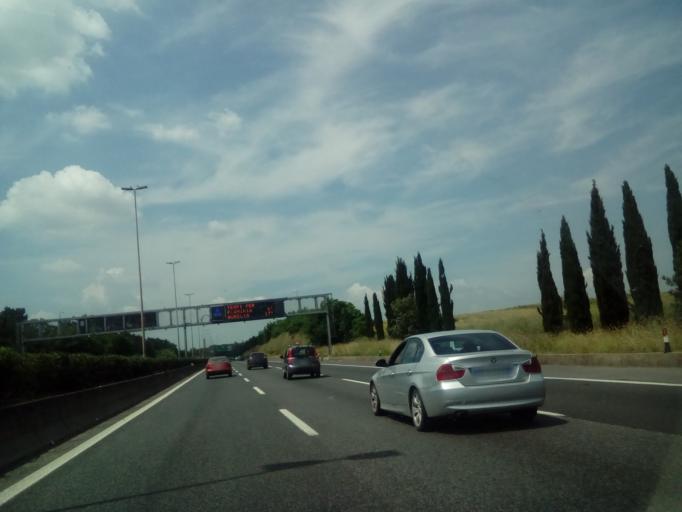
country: IT
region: Latium
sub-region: Citta metropolitana di Roma Capitale
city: Colle Verde
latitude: 41.9504
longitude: 12.5879
